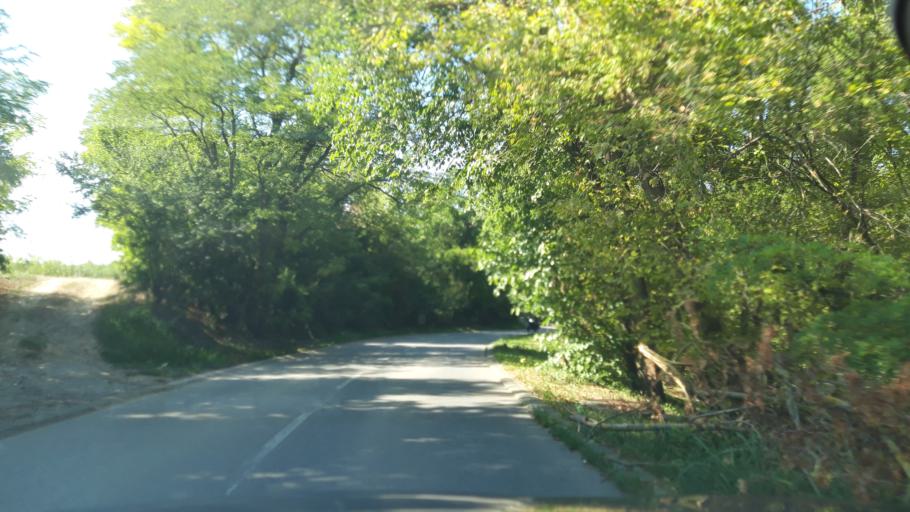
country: RS
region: Autonomna Pokrajina Vojvodina
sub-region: Sremski Okrug
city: Ruma
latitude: 45.0283
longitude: 19.8204
